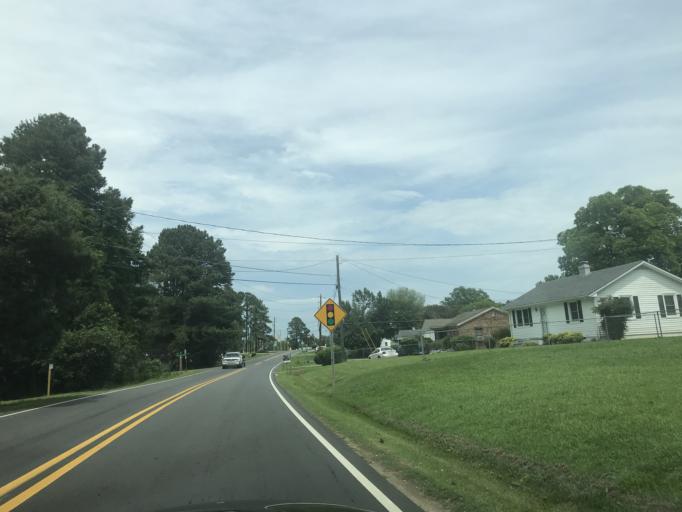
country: US
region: North Carolina
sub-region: Vance County
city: South Henderson
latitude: 36.2994
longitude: -78.4091
